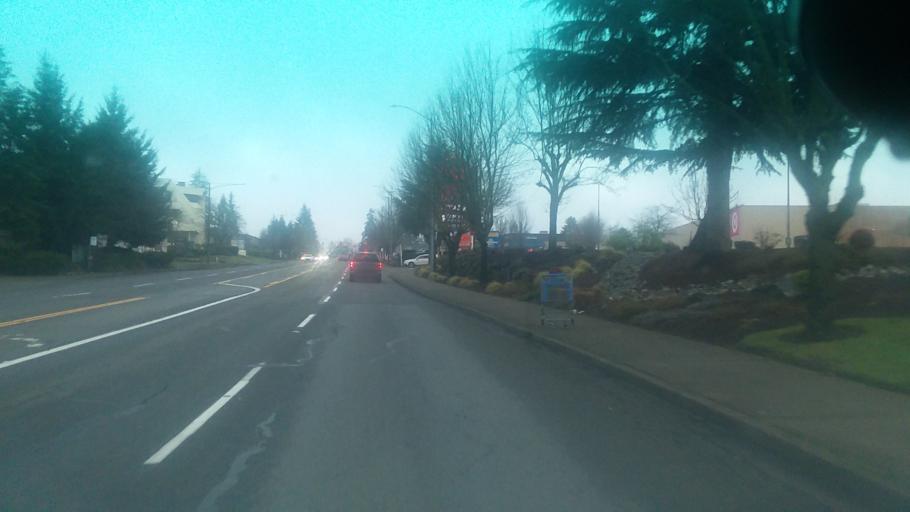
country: US
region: Washington
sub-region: Pierce County
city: Fircrest
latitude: 47.2365
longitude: -122.4816
